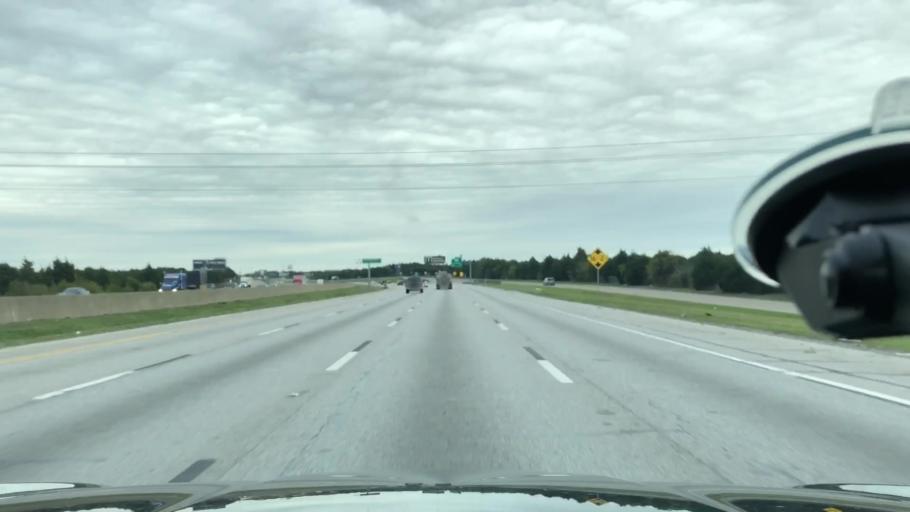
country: US
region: Texas
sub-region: Dallas County
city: Lancaster
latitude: 32.6421
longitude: -96.8038
